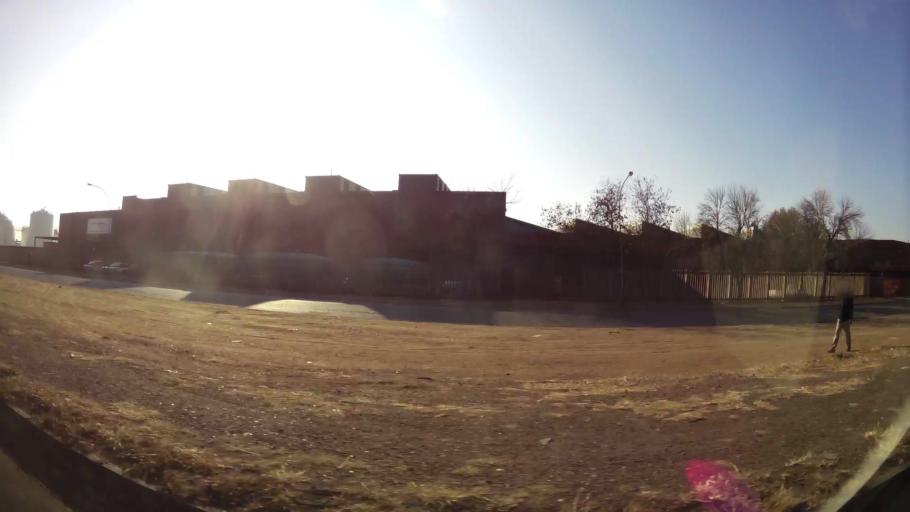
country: ZA
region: Orange Free State
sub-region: Mangaung Metropolitan Municipality
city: Bloemfontein
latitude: -29.1616
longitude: 26.2195
